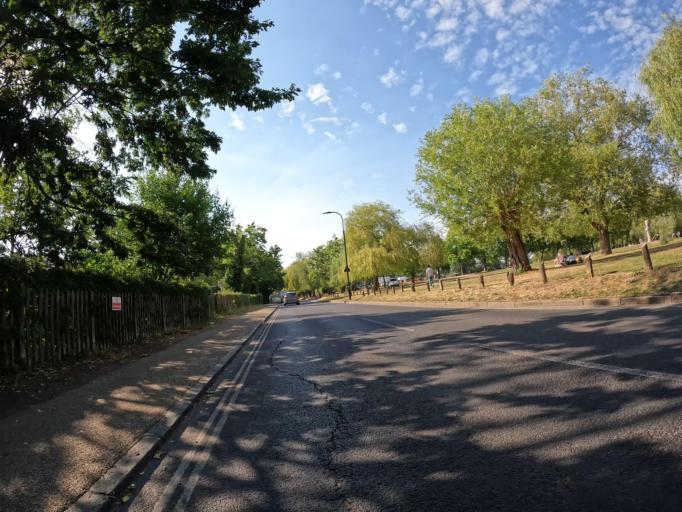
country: GB
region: England
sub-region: Greater London
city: Hadley Wood
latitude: 51.6692
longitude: -0.1630
